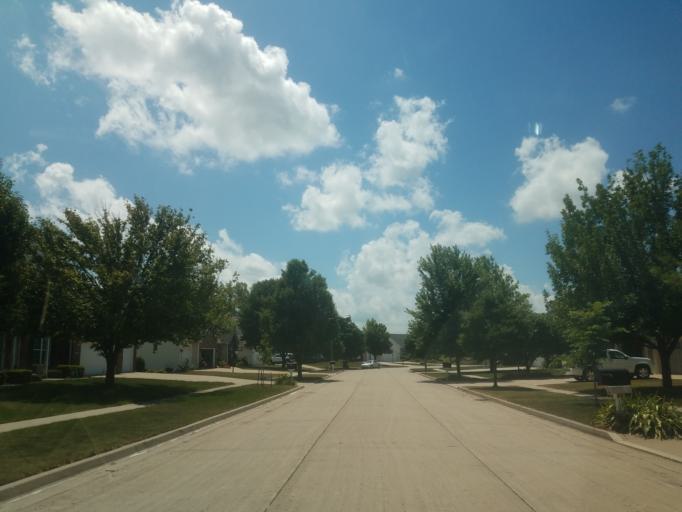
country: US
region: Illinois
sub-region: McLean County
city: Normal
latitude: 40.4966
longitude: -88.9138
